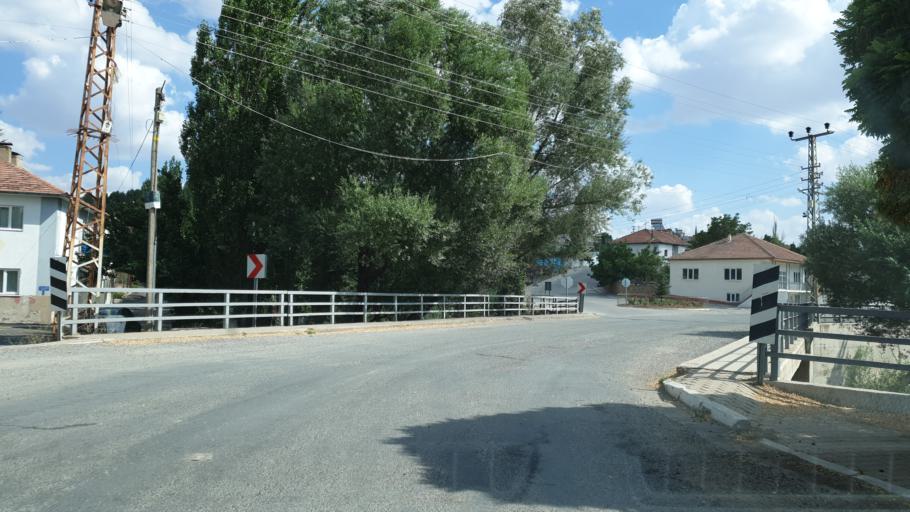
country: TR
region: Kayseri
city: Felahiye
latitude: 39.0942
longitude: 35.5630
